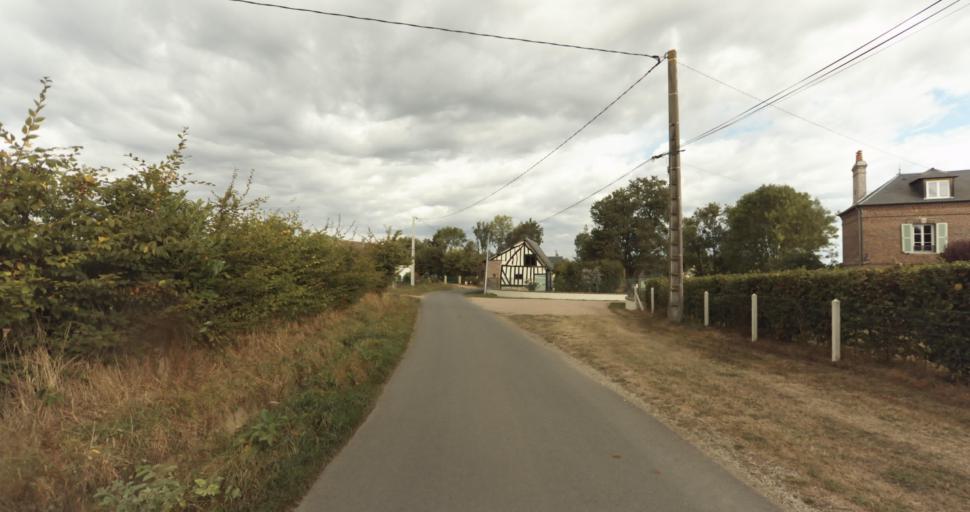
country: FR
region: Lower Normandy
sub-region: Departement de l'Orne
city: Vimoutiers
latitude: 48.9506
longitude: 0.2503
